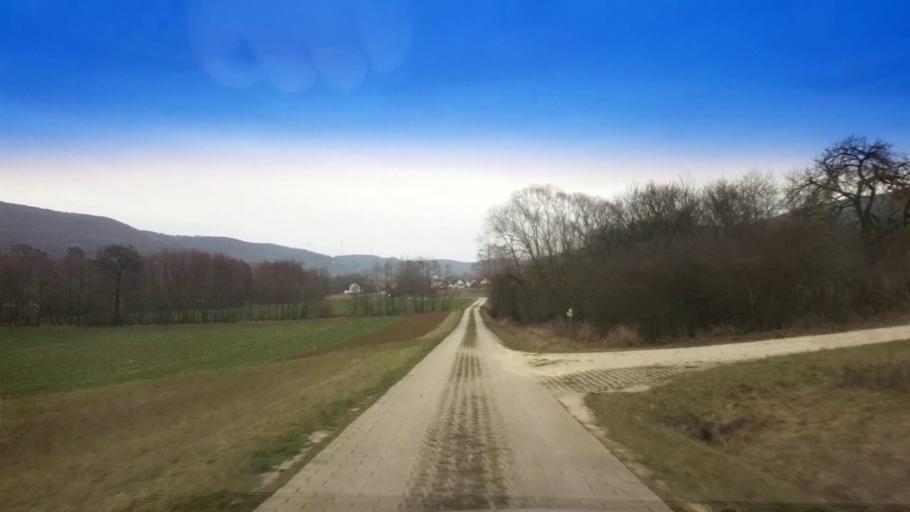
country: DE
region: Bavaria
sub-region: Upper Franconia
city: Litzendorf
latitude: 49.9140
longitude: 11.0326
